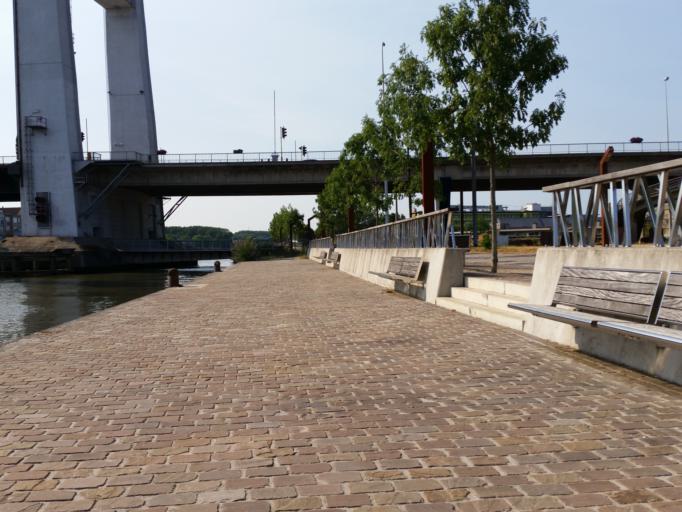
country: BE
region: Flanders
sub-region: Provincie Vlaams-Brabant
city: Vilvoorde
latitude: 50.9243
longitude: 4.4196
